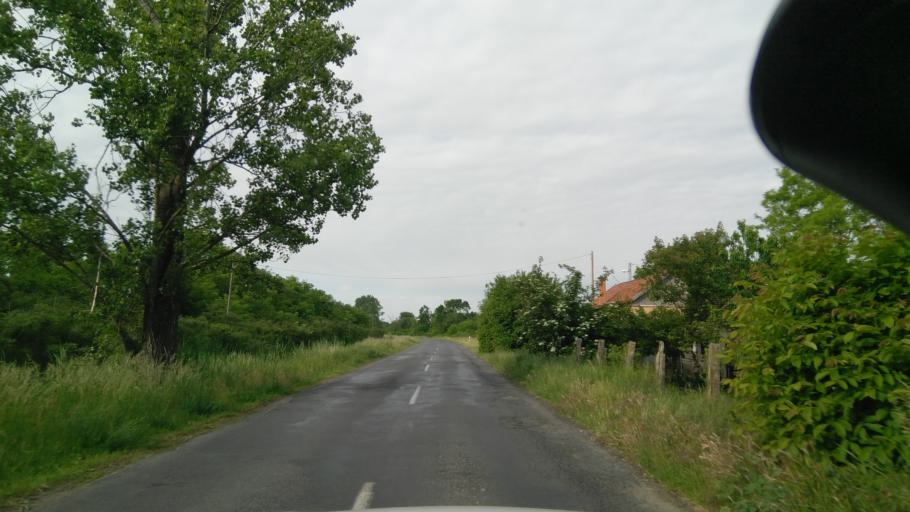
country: HU
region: Bekes
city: Elek
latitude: 46.5937
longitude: 21.2303
